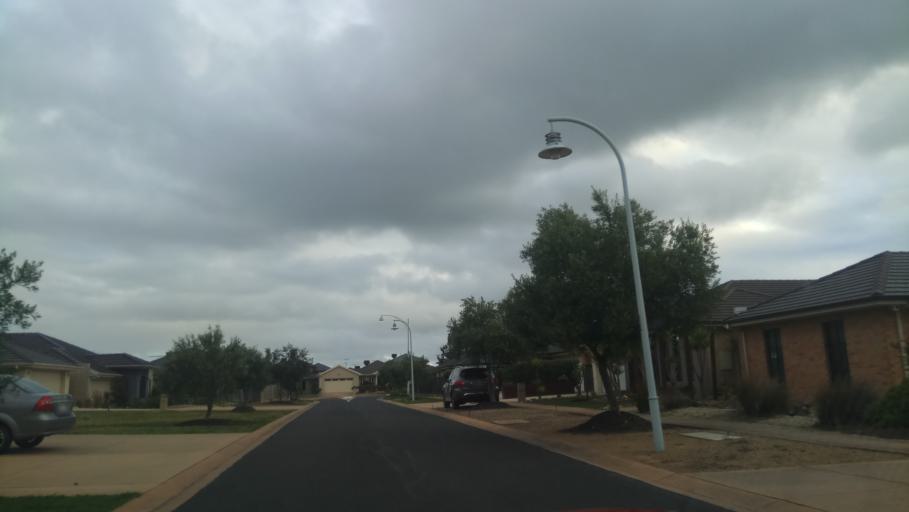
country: AU
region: Victoria
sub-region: Wyndham
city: Point Cook
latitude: -37.8998
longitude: 144.7577
